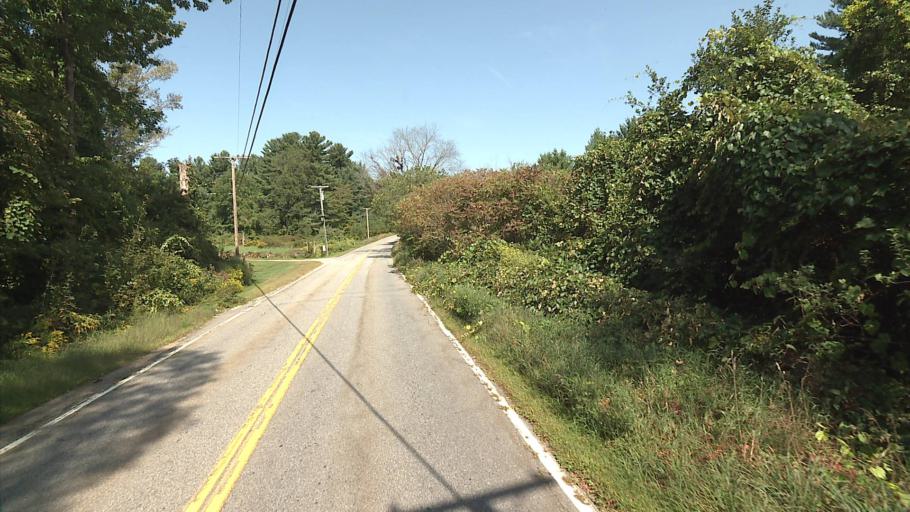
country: US
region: Connecticut
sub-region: Windham County
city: Quinebaug
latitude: 42.0040
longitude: -72.0005
